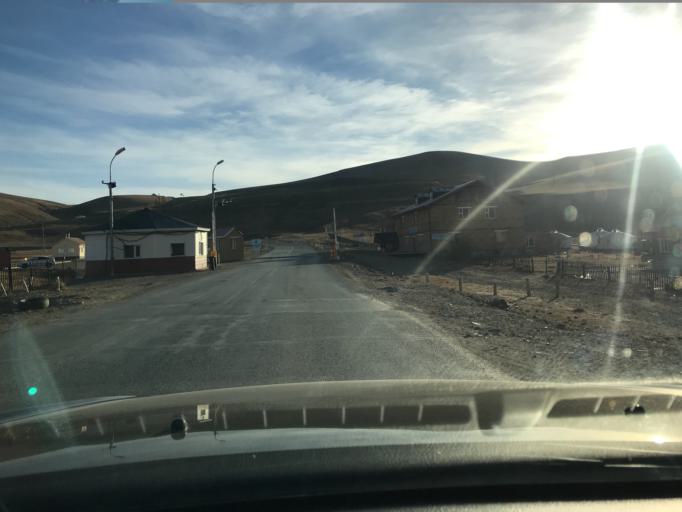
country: MN
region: Central Aimak
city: Dzuunmod
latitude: 47.8170
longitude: 107.3295
